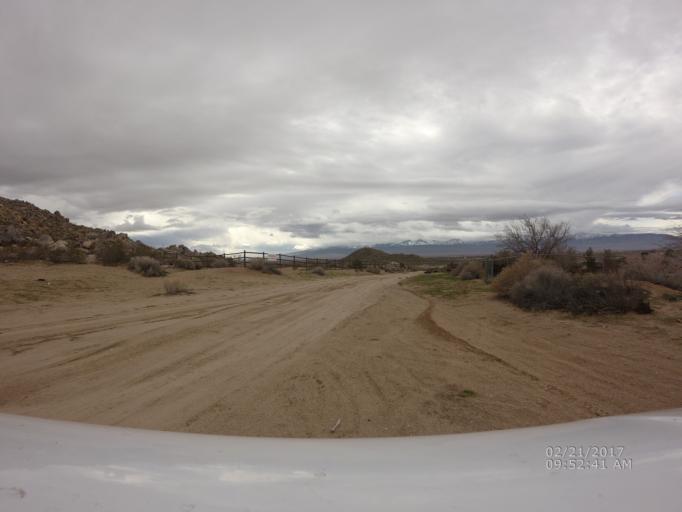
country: US
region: California
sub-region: Los Angeles County
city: Lake Los Angeles
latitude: 34.6021
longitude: -117.8182
